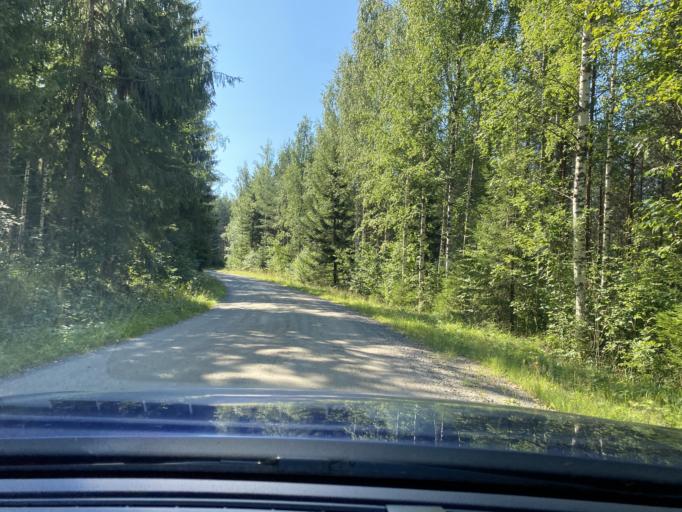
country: FI
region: Central Finland
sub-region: Jyvaeskylae
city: Korpilahti
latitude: 61.8736
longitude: 25.4136
